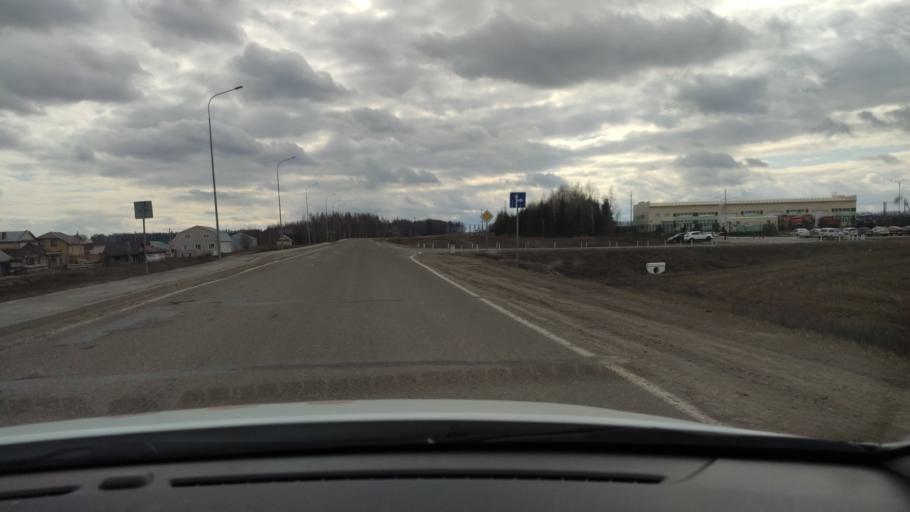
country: RU
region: Tatarstan
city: Vysokaya Gora
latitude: 56.1129
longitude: 49.1862
